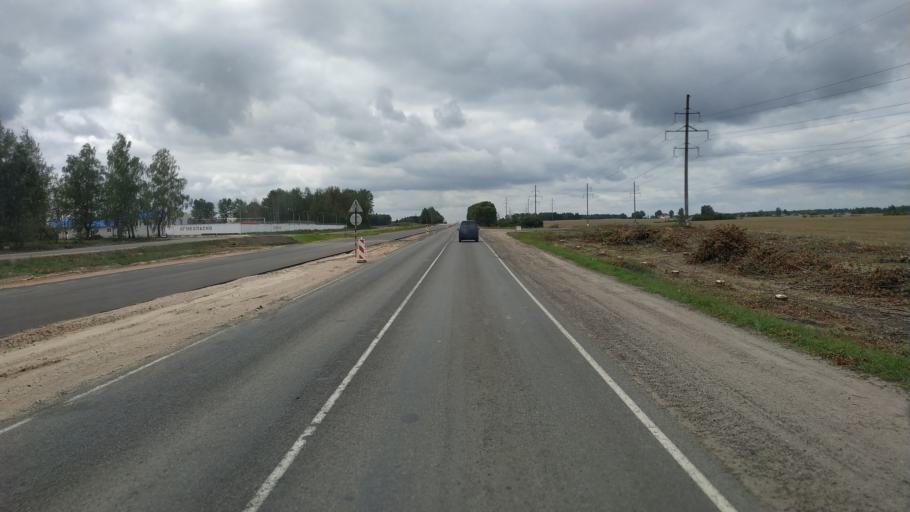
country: BY
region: Mogilev
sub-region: Mahilyowski Rayon
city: Kadino
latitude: 53.8684
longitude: 30.4700
